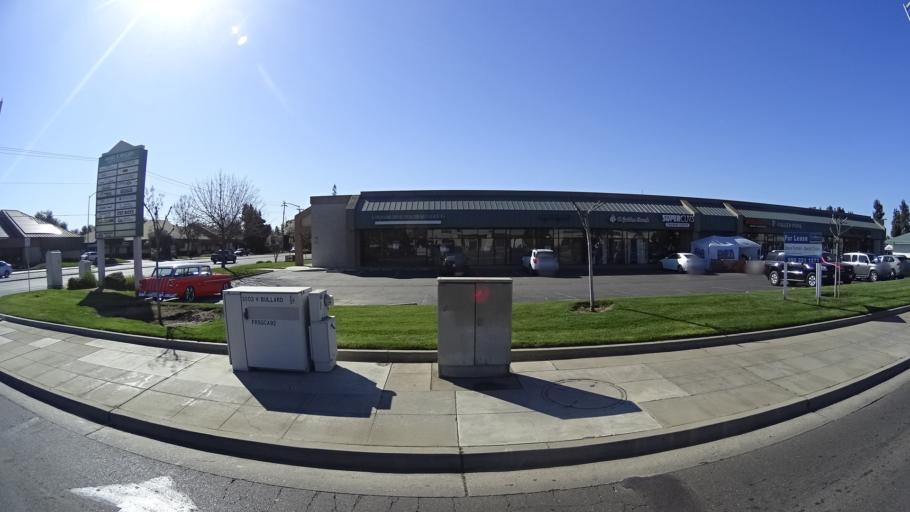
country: US
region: California
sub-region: Fresno County
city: Fresno
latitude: 36.8227
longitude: -119.8449
